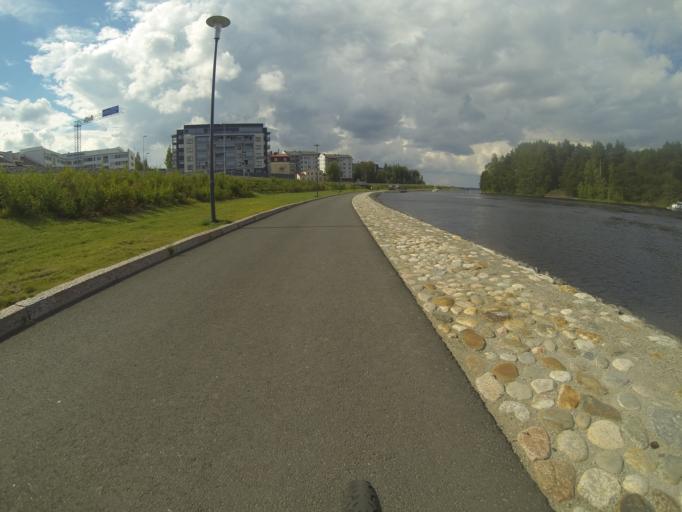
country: FI
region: Southern Savonia
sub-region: Savonlinna
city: Savonlinna
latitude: 61.8700
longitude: 28.8847
